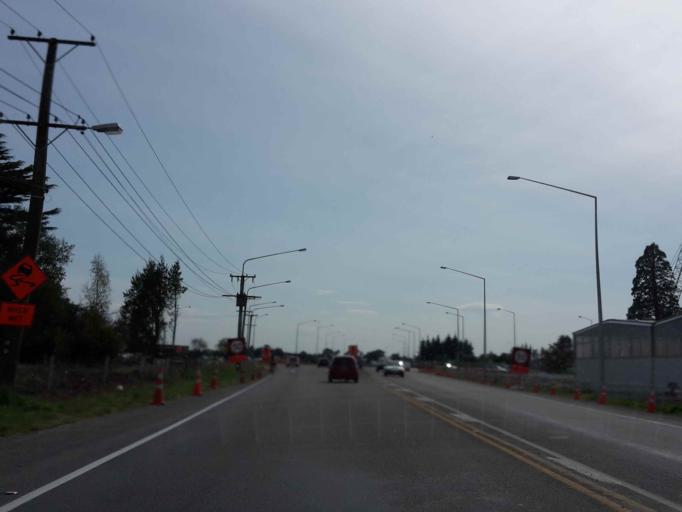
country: NZ
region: Canterbury
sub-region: Christchurch City
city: Christchurch
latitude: -43.4803
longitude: 172.5557
